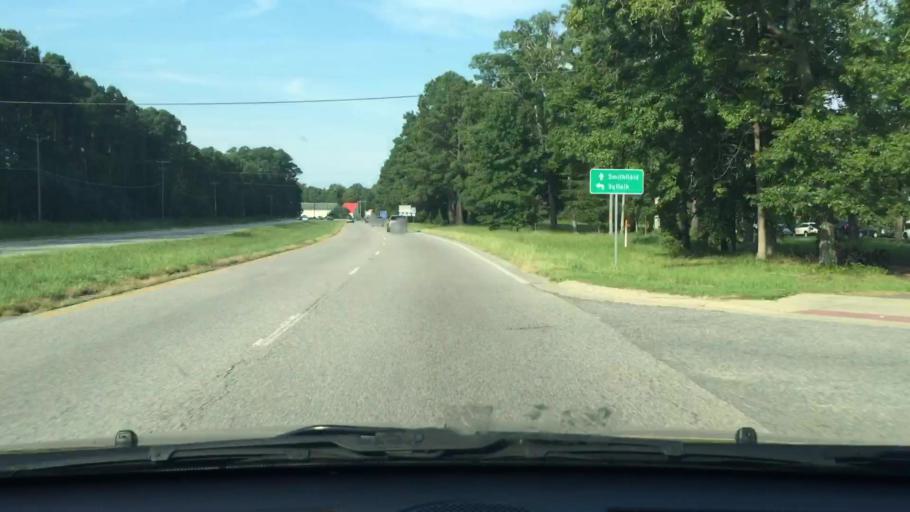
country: US
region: Virginia
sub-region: Isle of Wight County
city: Carrollton
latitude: 36.9396
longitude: -76.5744
